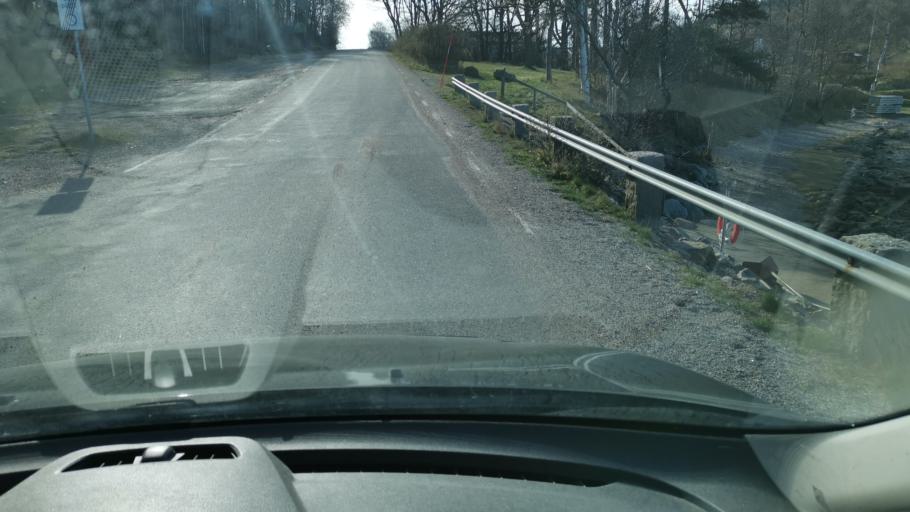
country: SE
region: Vaestra Goetaland
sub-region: Lysekils Kommun
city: Brastad
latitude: 58.3458
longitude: 11.5889
